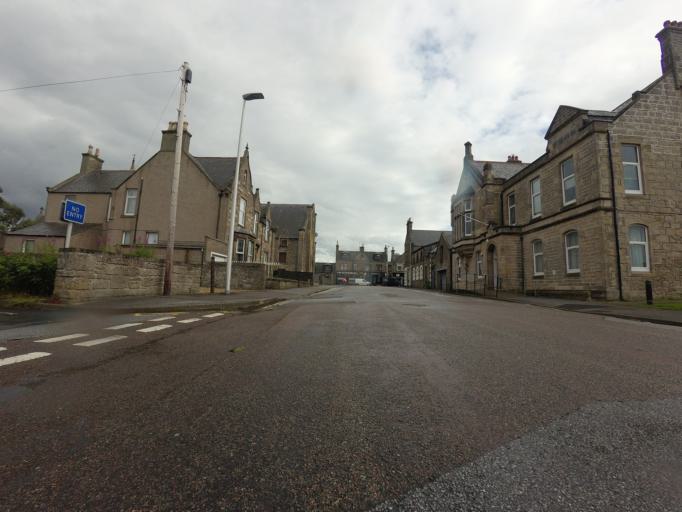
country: GB
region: Scotland
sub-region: Moray
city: Buckie
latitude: 57.6764
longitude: -2.9672
